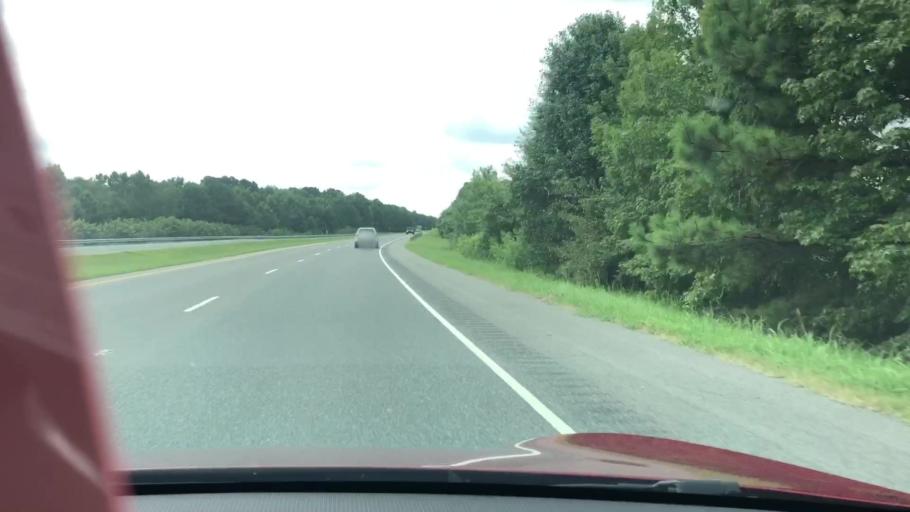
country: US
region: North Carolina
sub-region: Currituck County
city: Moyock
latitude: 36.6011
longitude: -76.1994
